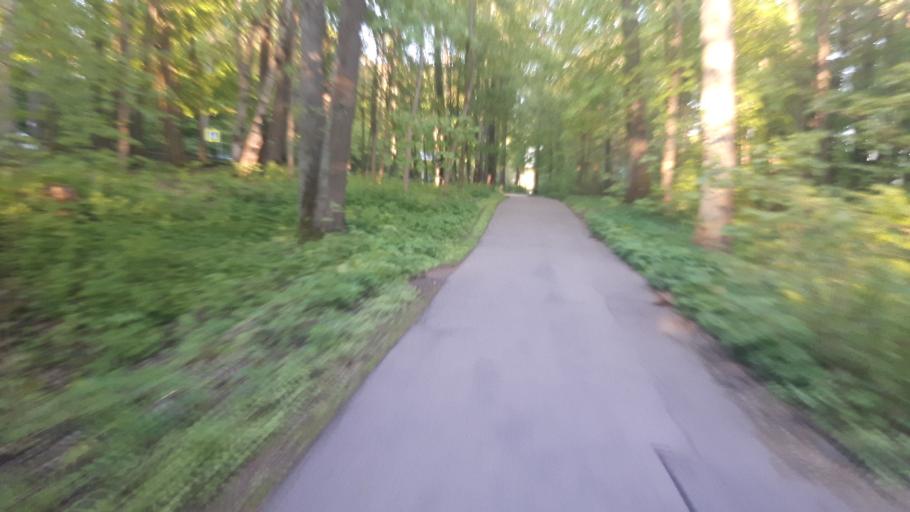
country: RU
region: St.-Petersburg
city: Zelenogorsk
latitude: 60.1922
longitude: 29.6386
